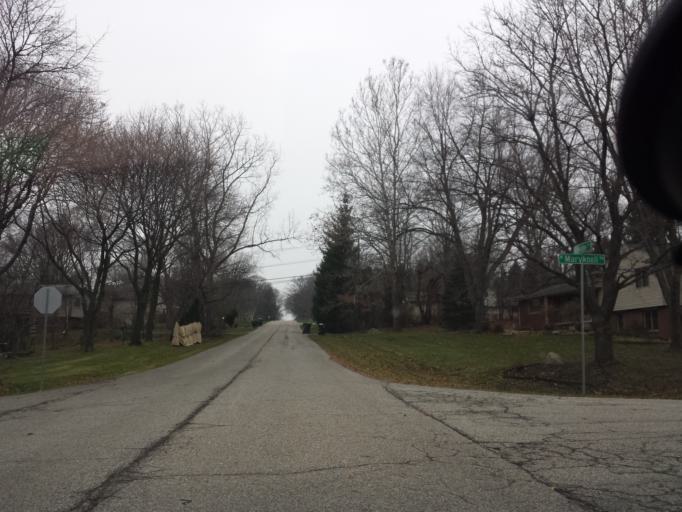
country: US
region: Michigan
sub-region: Oakland County
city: Rochester Hills
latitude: 42.6757
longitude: -83.1874
